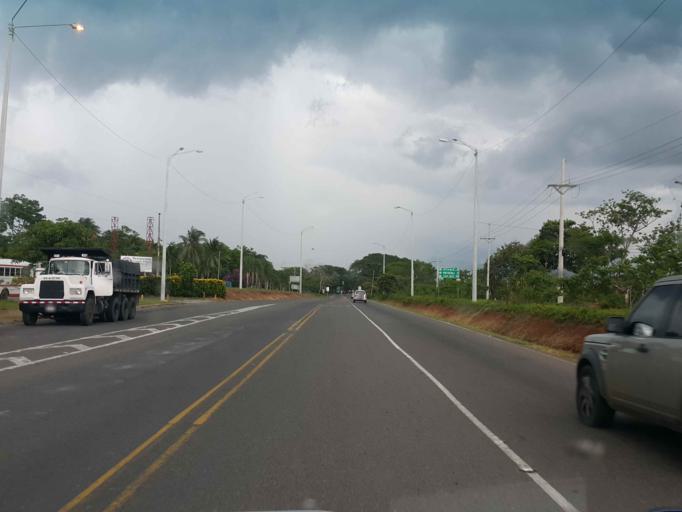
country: CR
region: Puntarenas
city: Miramar
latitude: 10.0941
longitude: -84.8205
